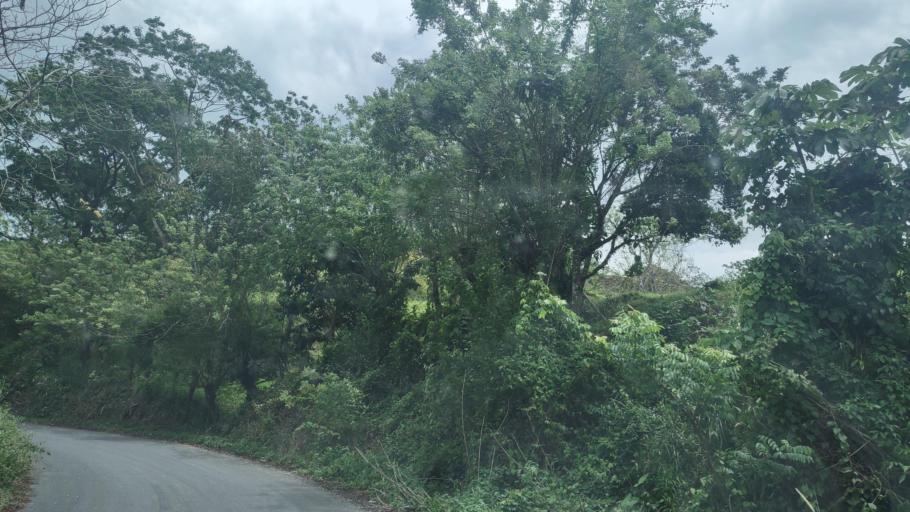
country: MX
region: Tabasco
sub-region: Huimanguillo
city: Francisco Rueda
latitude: 17.5238
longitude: -94.1370
